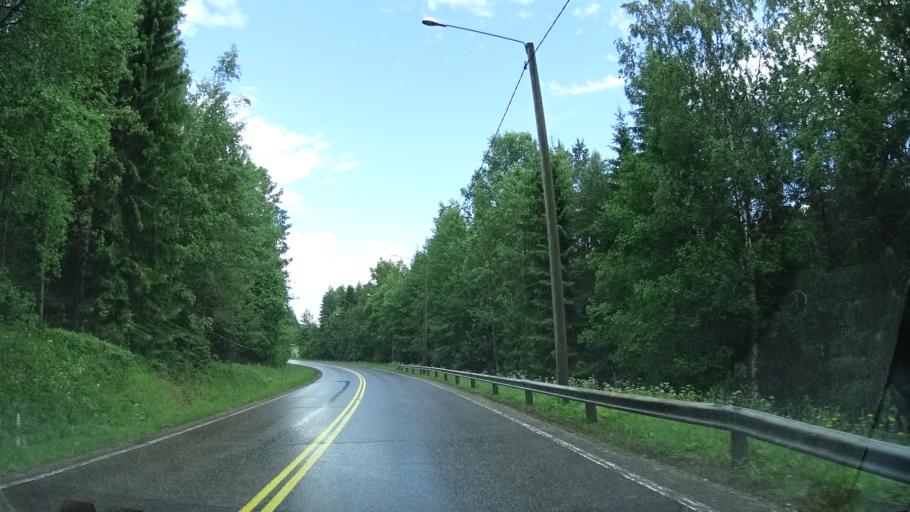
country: FI
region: Uusimaa
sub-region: Helsinki
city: Espoo
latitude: 60.3363
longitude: 24.6542
